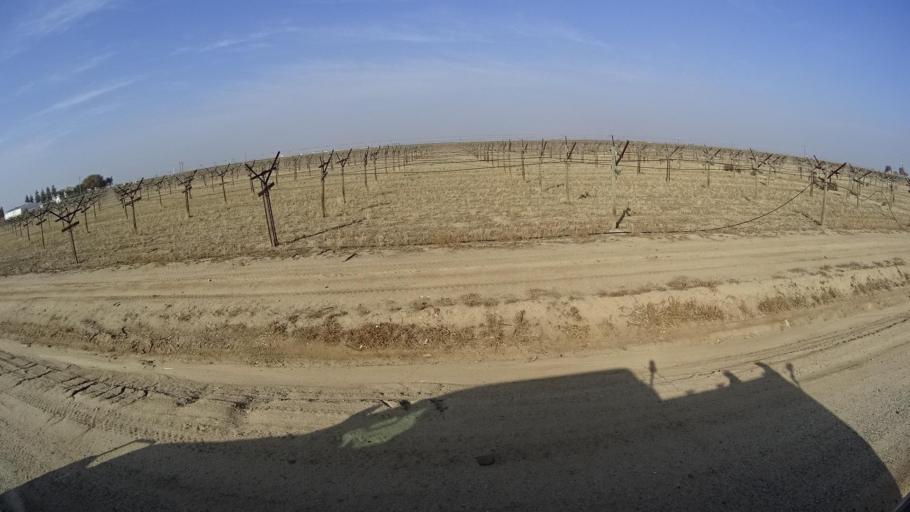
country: US
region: California
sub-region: Tulare County
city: Richgrove
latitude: 35.7761
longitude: -119.1409
